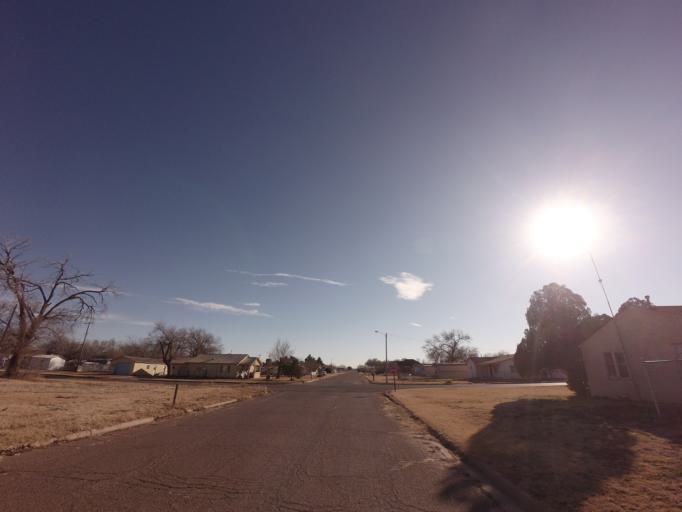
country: US
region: New Mexico
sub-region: Curry County
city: Clovis
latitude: 34.4032
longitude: -103.1852
